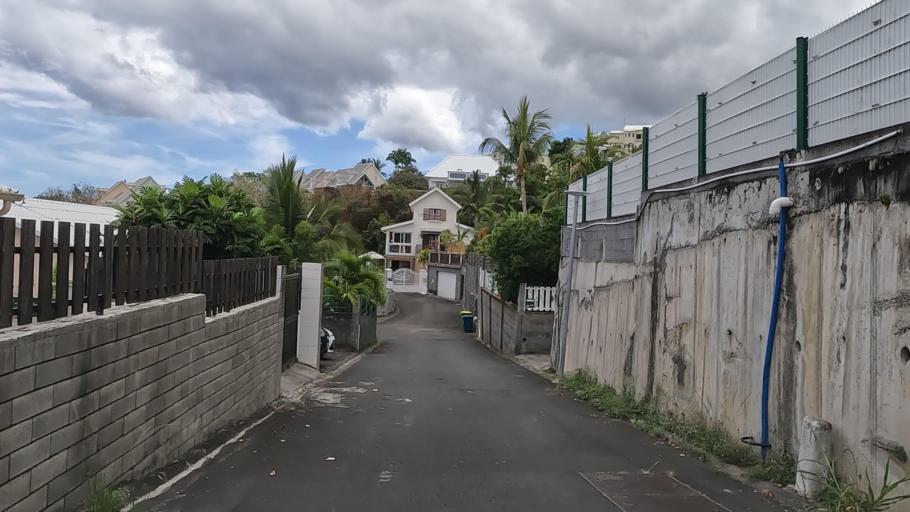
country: RE
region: Reunion
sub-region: Reunion
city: La Possession
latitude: -20.9590
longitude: 55.3368
